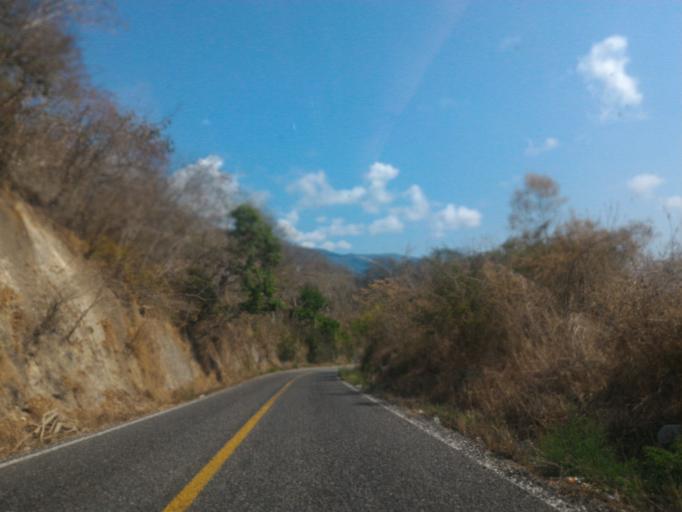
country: MX
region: Michoacan
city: Coahuayana Viejo
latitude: 18.4674
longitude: -103.5485
